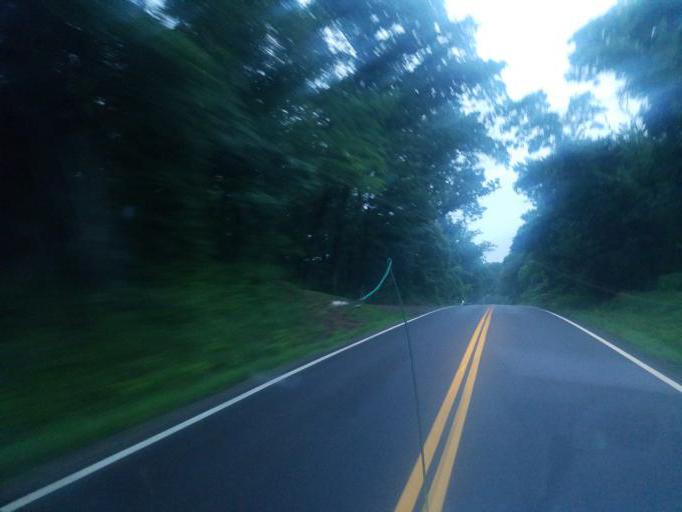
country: US
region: Ohio
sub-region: Carroll County
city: Carrollton
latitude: 40.5043
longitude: -81.0362
